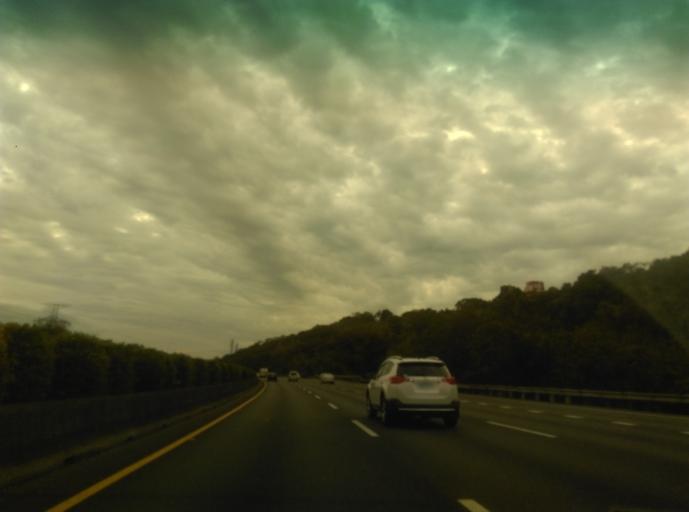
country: TW
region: Taiwan
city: Daxi
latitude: 24.9210
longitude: 121.2982
